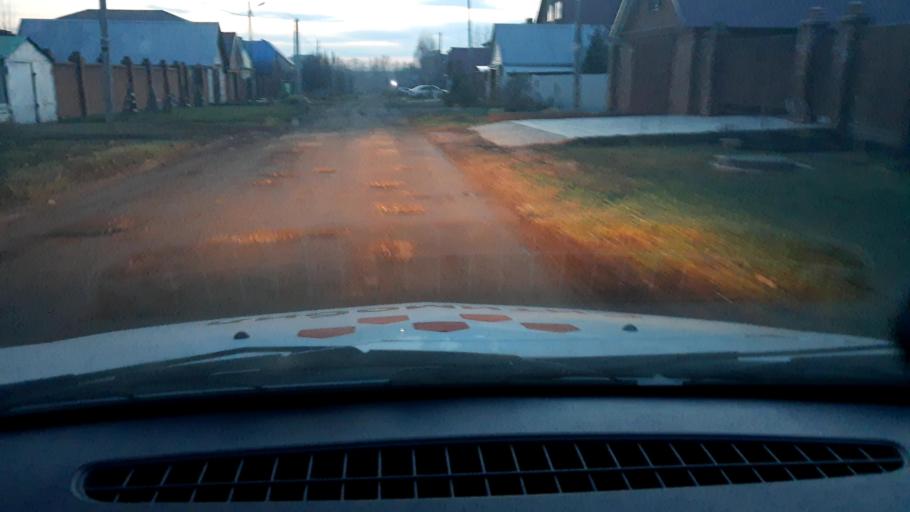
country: RU
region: Bashkortostan
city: Iglino
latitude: 54.7801
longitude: 56.2378
